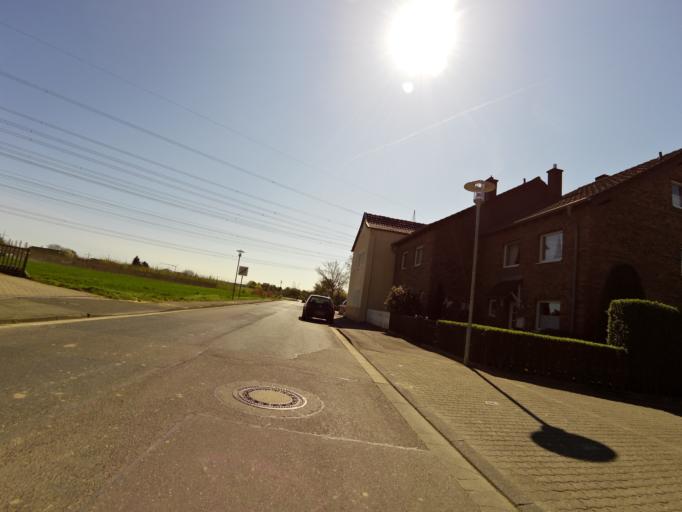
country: DE
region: North Rhine-Westphalia
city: Meckenheim
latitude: 50.6474
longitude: 7.0070
